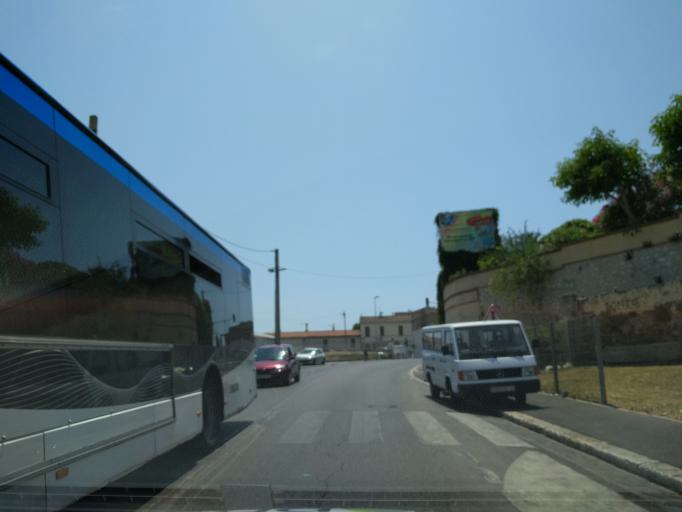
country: FR
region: Provence-Alpes-Cote d'Azur
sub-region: Departement des Bouches-du-Rhone
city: Marseille 14
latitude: 43.3312
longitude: 5.3591
